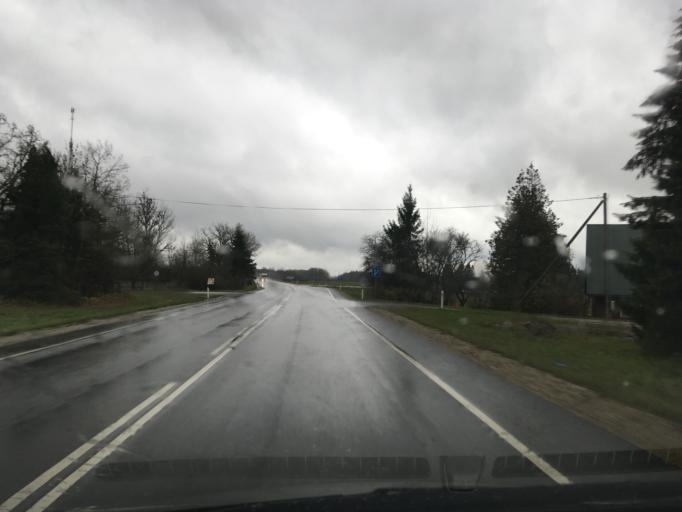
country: EE
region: Laeaene
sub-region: Lihula vald
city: Lihula
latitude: 58.7681
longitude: 23.9882
